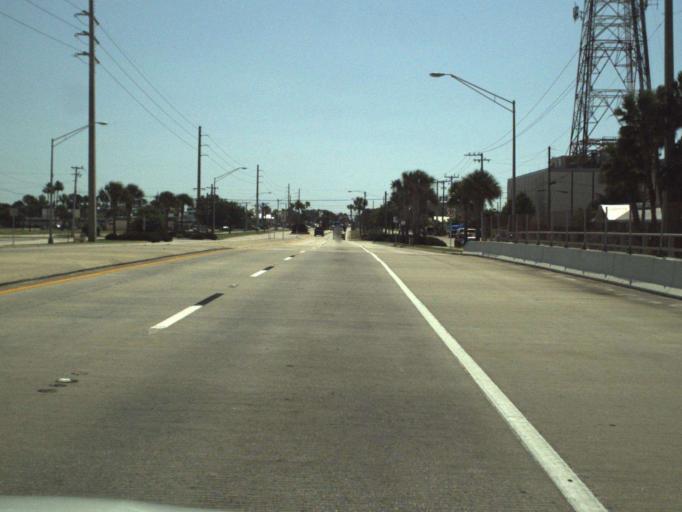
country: US
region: Florida
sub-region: Brevard County
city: Cocoa Beach
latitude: 28.3578
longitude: -80.6154
